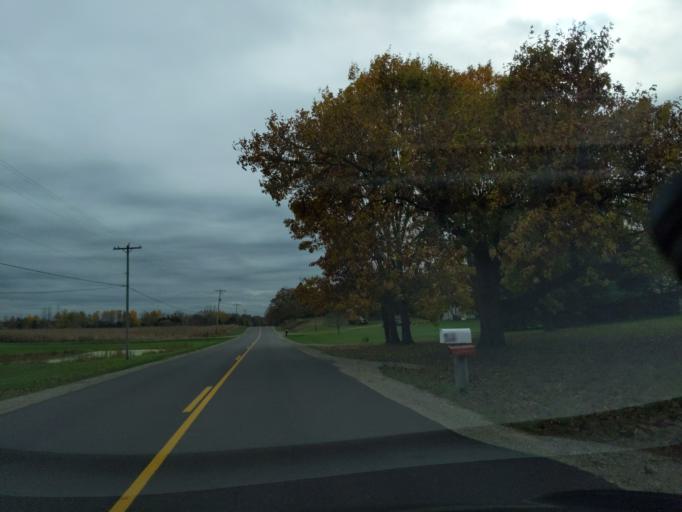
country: US
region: Michigan
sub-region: Eaton County
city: Eaton Rapids
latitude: 42.5340
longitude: -84.6212
